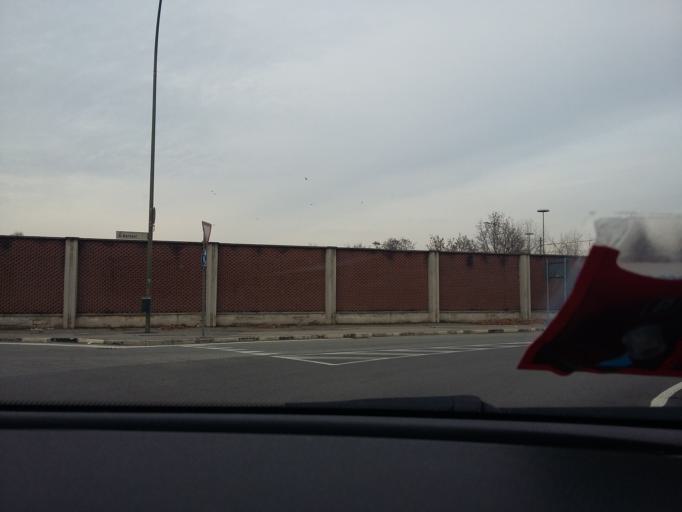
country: IT
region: Piedmont
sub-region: Provincia di Torino
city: Fornaci
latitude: 45.0342
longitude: 7.6055
